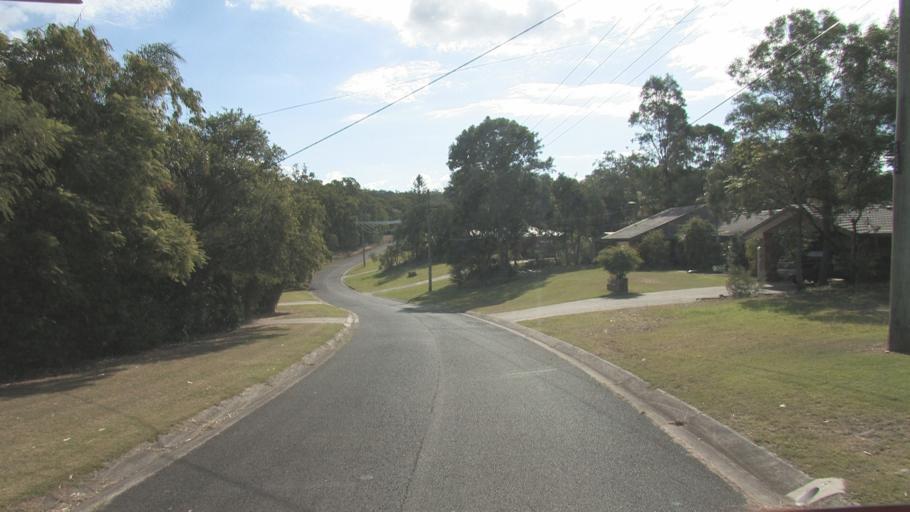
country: AU
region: Queensland
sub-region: Logan
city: Windaroo
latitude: -27.7344
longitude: 153.1896
